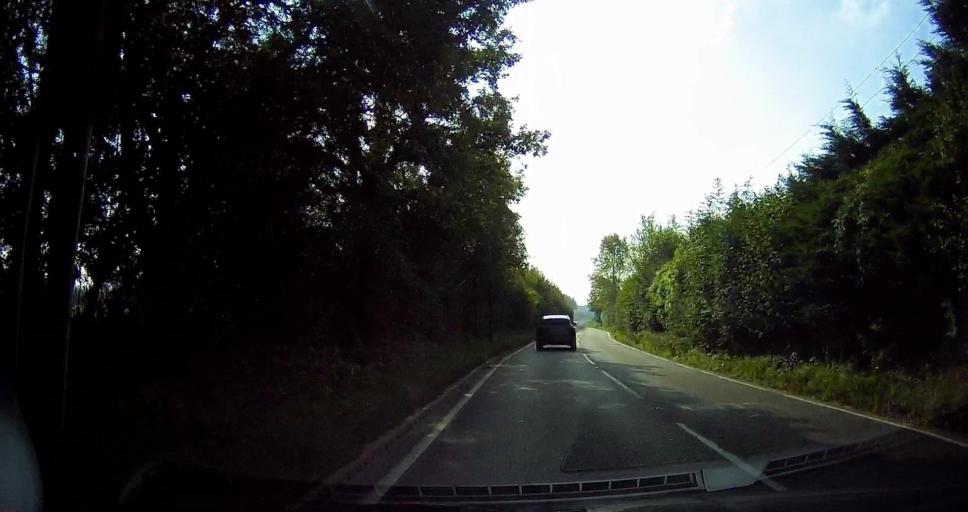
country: GB
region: England
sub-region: Kent
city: Kennington
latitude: 51.1830
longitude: 0.9075
